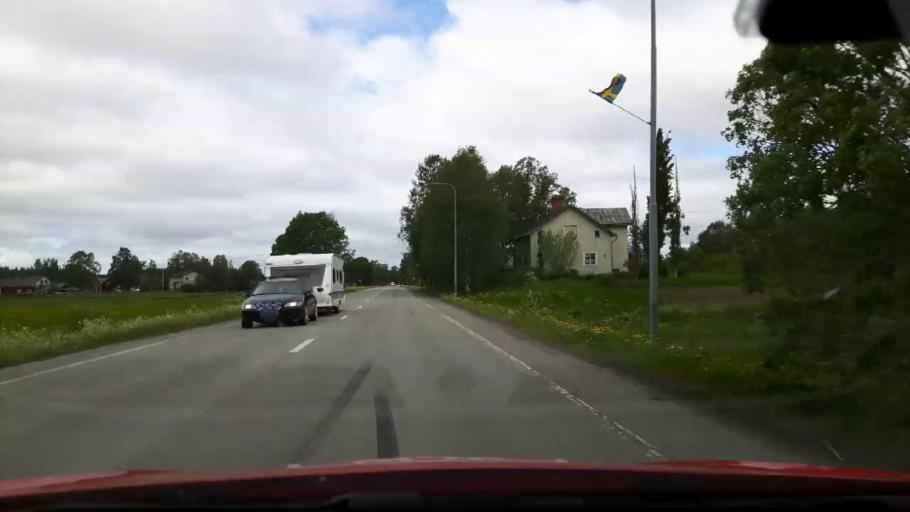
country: SE
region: Jaemtland
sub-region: Krokoms Kommun
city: Krokom
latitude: 63.3073
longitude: 14.4659
